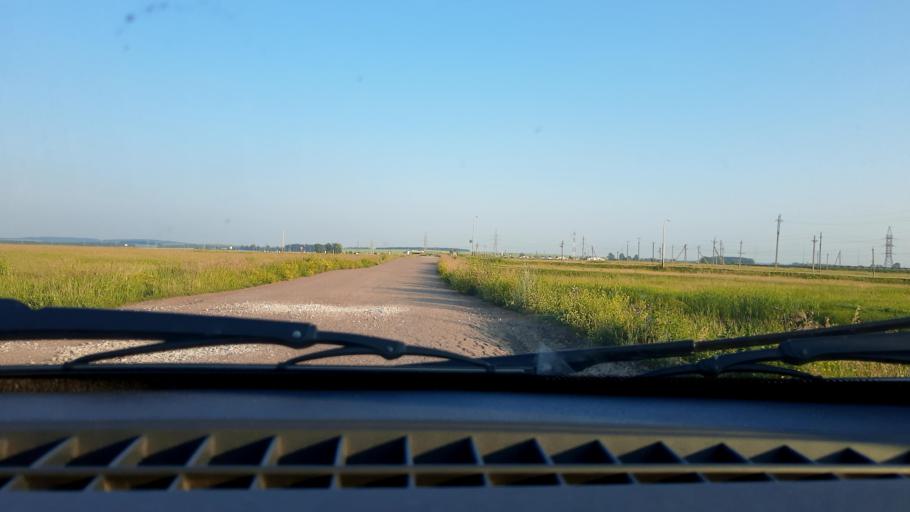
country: RU
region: Bashkortostan
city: Asanovo
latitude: 54.9066
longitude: 55.6278
